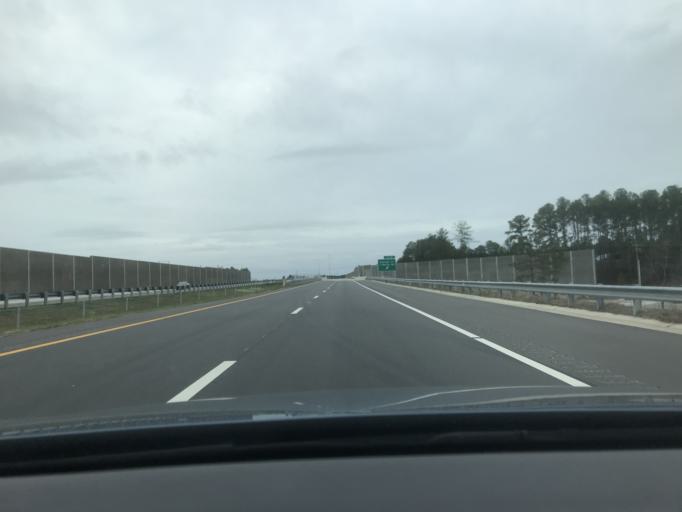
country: US
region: North Carolina
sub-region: Cumberland County
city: Fort Bragg
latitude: 35.1072
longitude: -79.0018
